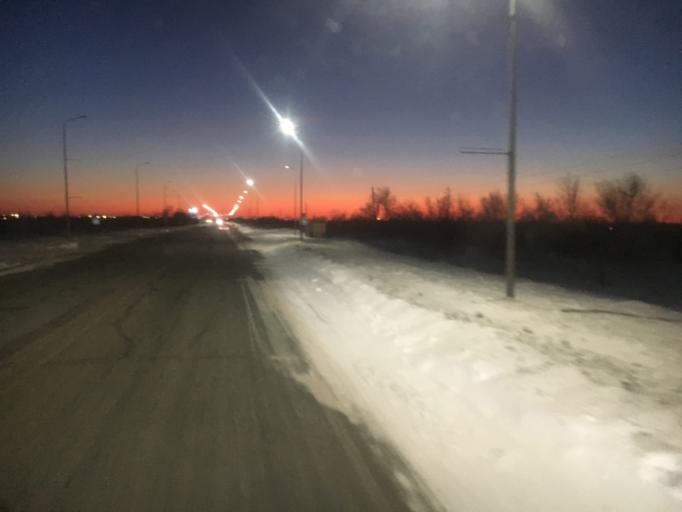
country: KZ
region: Batys Qazaqstan
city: Oral
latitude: 51.1657
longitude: 51.5233
